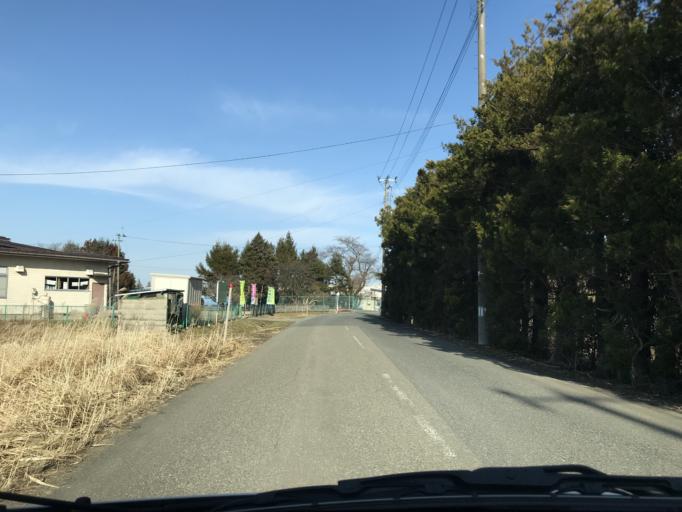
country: JP
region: Iwate
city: Kitakami
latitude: 39.2950
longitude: 141.0504
